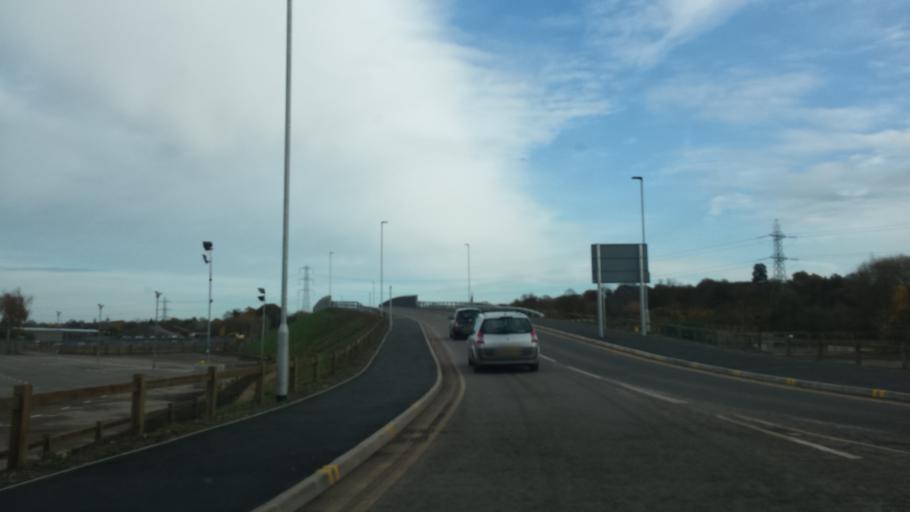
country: GB
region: England
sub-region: Hertfordshire
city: Watford
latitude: 51.6469
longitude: -0.4009
